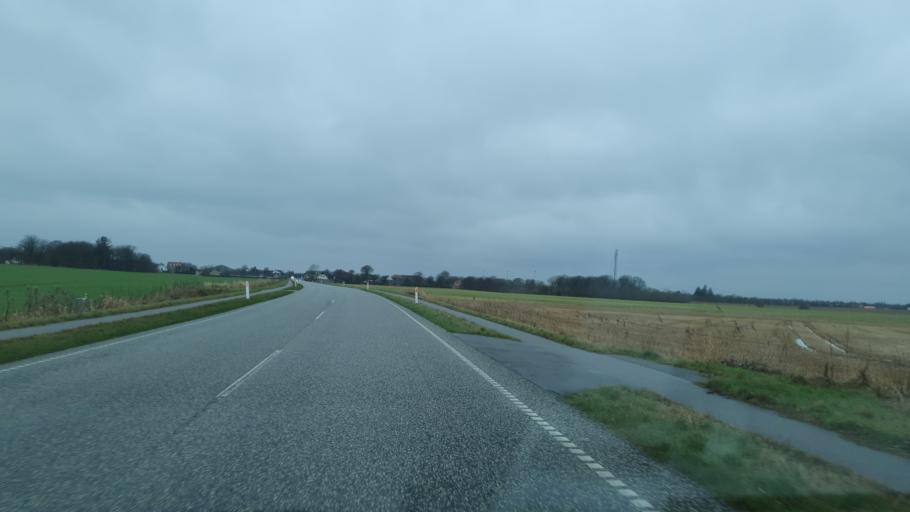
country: DK
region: North Denmark
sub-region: Jammerbugt Kommune
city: Fjerritslev
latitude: 57.1013
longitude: 9.1370
